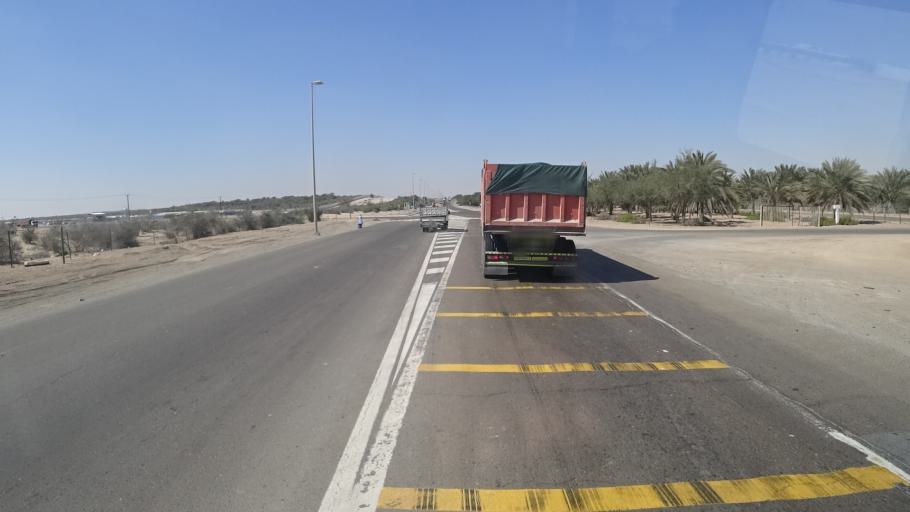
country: AE
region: Abu Dhabi
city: Abu Dhabi
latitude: 24.2240
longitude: 54.7540
